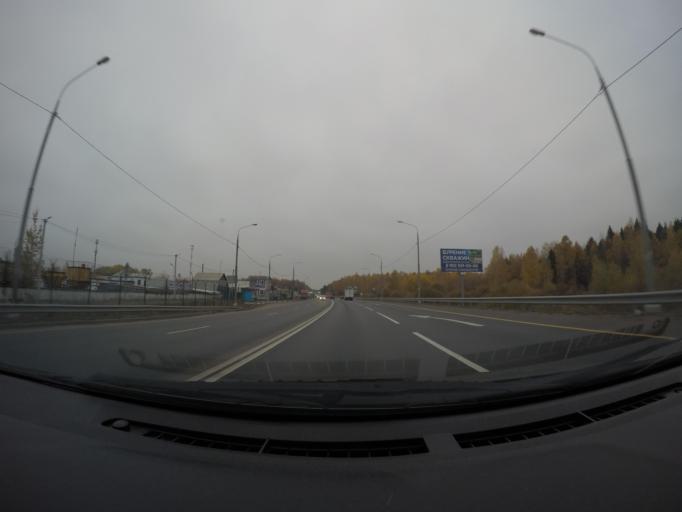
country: RU
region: Moskovskaya
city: Bronnitsy
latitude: 55.4077
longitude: 38.2307
